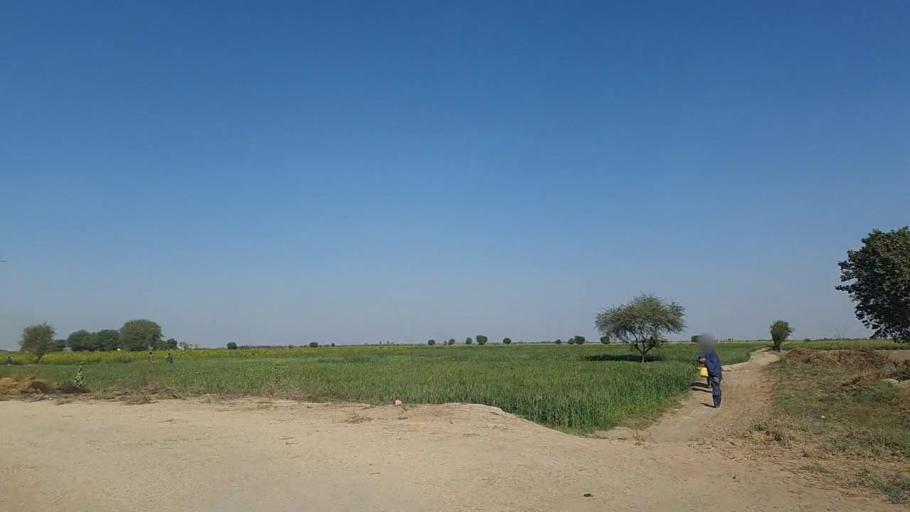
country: PK
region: Sindh
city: Naukot
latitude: 25.0168
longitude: 69.3594
